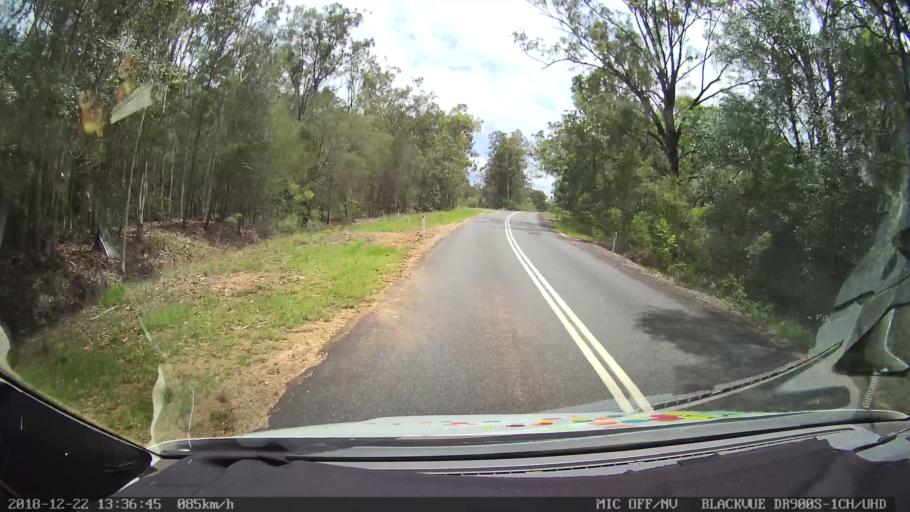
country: AU
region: New South Wales
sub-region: Clarence Valley
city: Coutts Crossing
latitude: -29.8829
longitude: 152.7924
